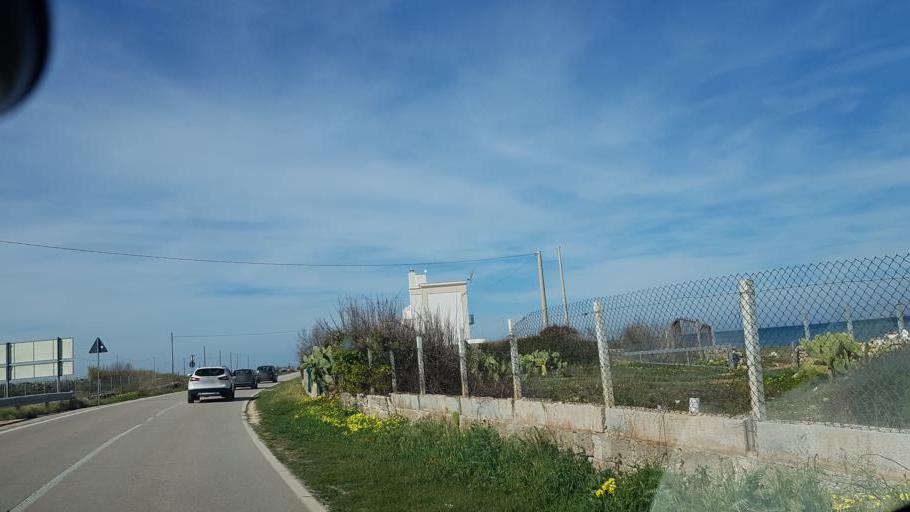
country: IT
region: Apulia
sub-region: Provincia di Brindisi
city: Pezze di Greco
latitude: 40.8544
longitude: 17.4427
